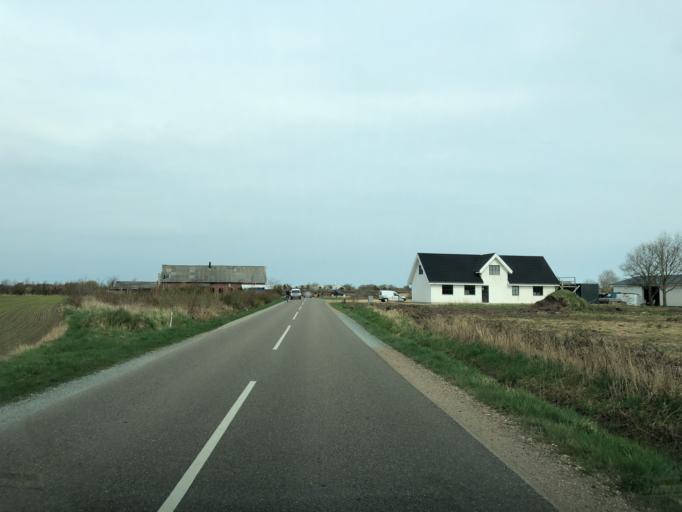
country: DK
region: South Denmark
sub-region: Varde Kommune
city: Oksbol
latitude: 55.7757
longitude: 8.2723
